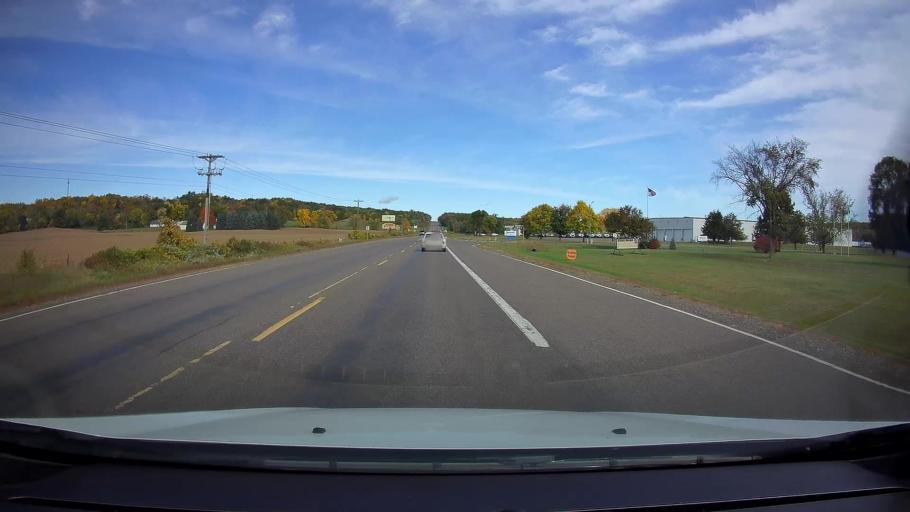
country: US
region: Wisconsin
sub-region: Polk County
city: Saint Croix Falls
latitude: 45.3606
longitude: -92.6366
